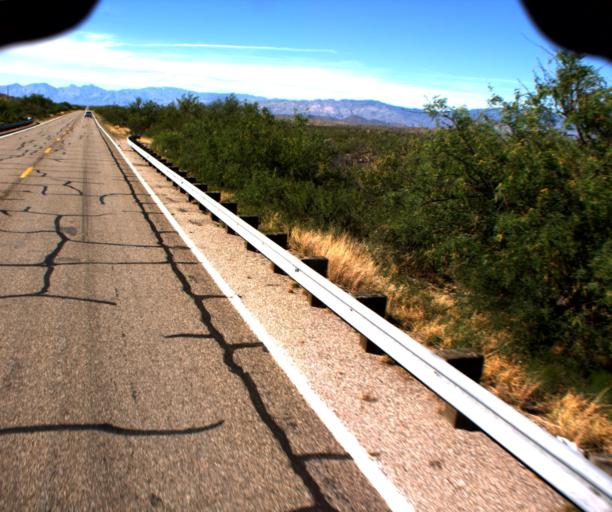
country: US
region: Arizona
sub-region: Pima County
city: Corona de Tucson
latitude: 31.9422
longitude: -110.6634
